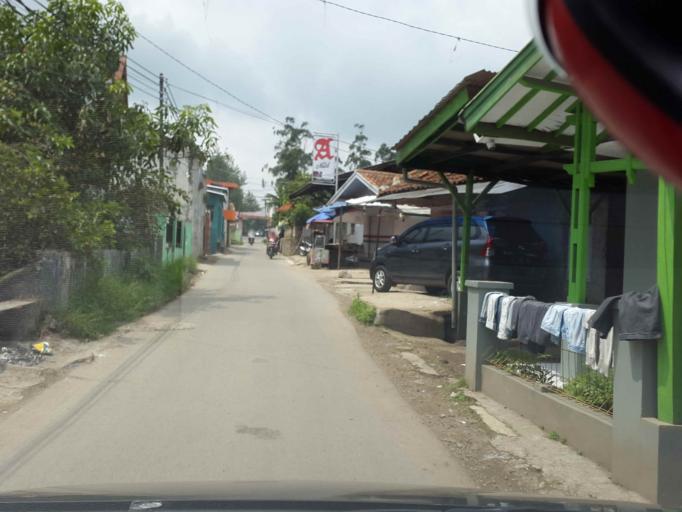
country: ID
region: West Java
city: Lembang
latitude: -6.8065
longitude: 107.6399
